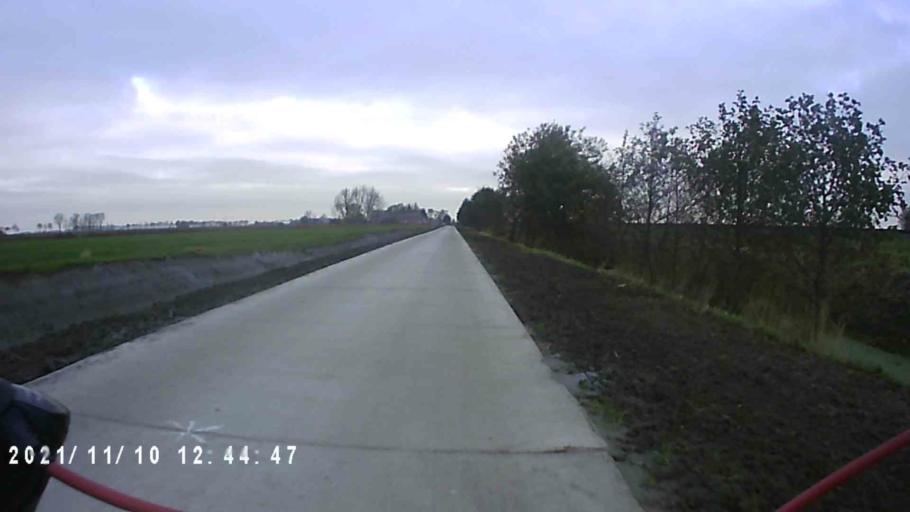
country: NL
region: Groningen
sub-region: Gemeente Groningen
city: Korrewegwijk
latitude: 53.2586
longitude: 6.5488
